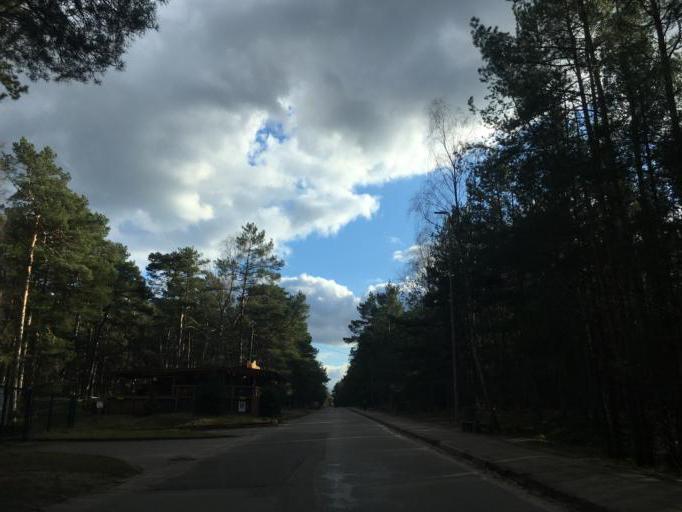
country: PL
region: Pomeranian Voivodeship
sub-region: Powiat gdanski
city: Cedry Wielkie
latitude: 54.3491
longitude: 18.8343
